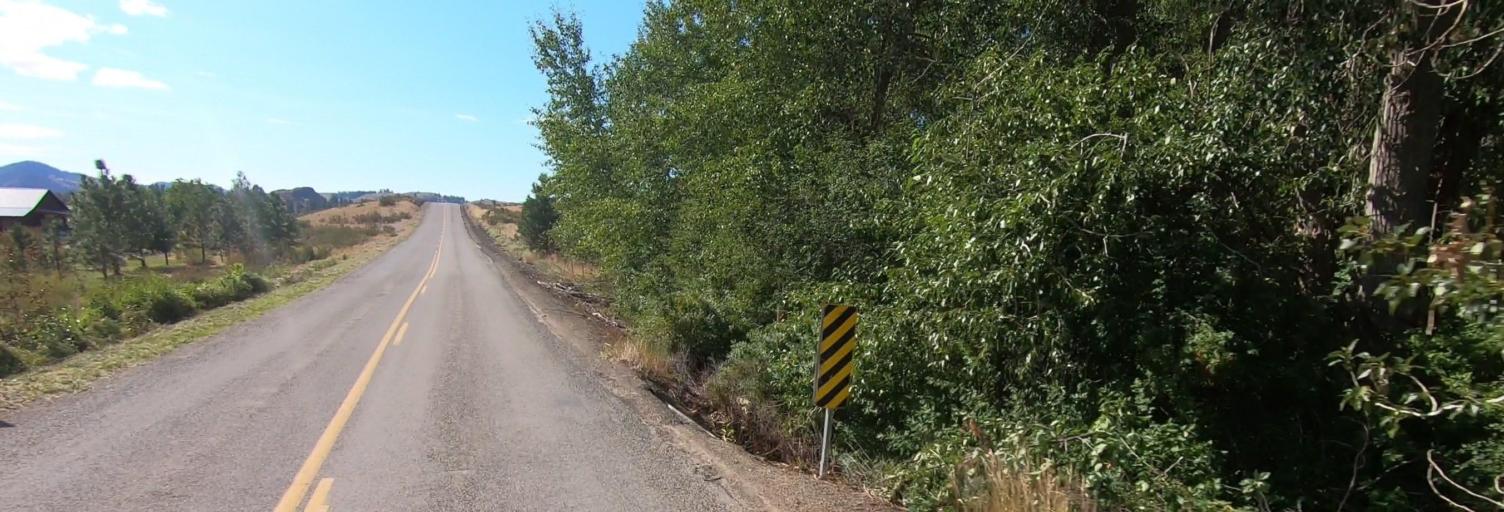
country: US
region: Washington
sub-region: Okanogan County
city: Brewster
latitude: 48.5218
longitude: -120.1773
